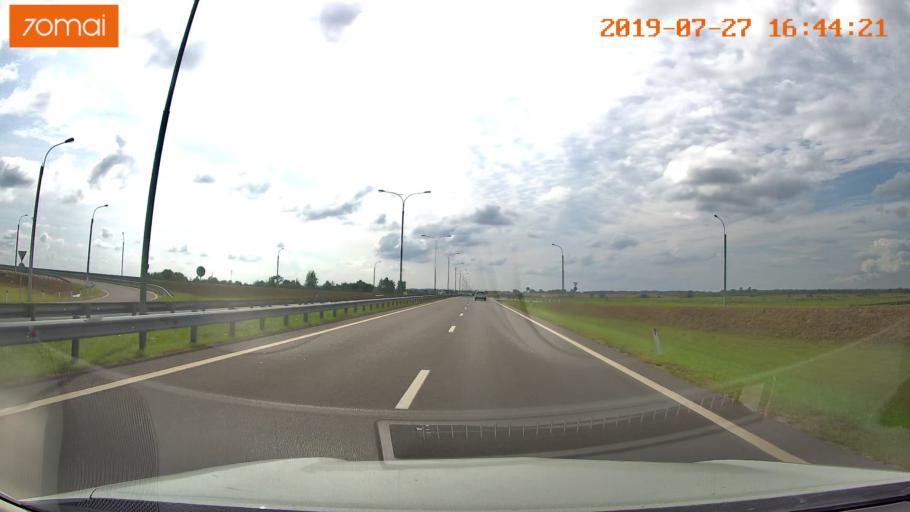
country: RU
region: Kaliningrad
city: Gvardeysk
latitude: 54.6725
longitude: 21.0790
